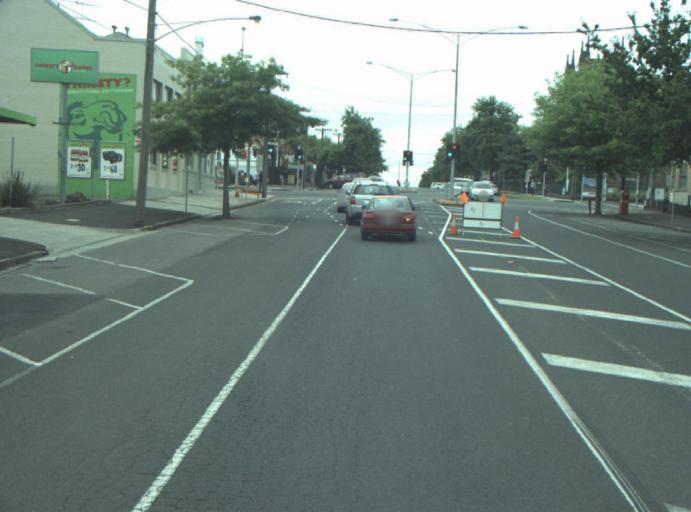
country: AU
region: Victoria
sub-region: Greater Geelong
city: Geelong
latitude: -38.1513
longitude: 144.3618
